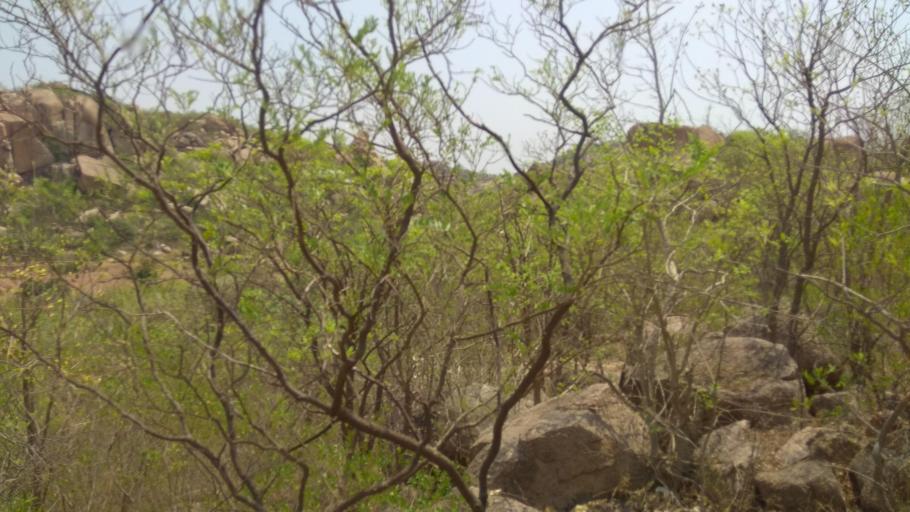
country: IN
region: Telangana
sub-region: Mahbubnagar
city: Farrukhnagar
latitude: 16.8861
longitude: 78.4979
